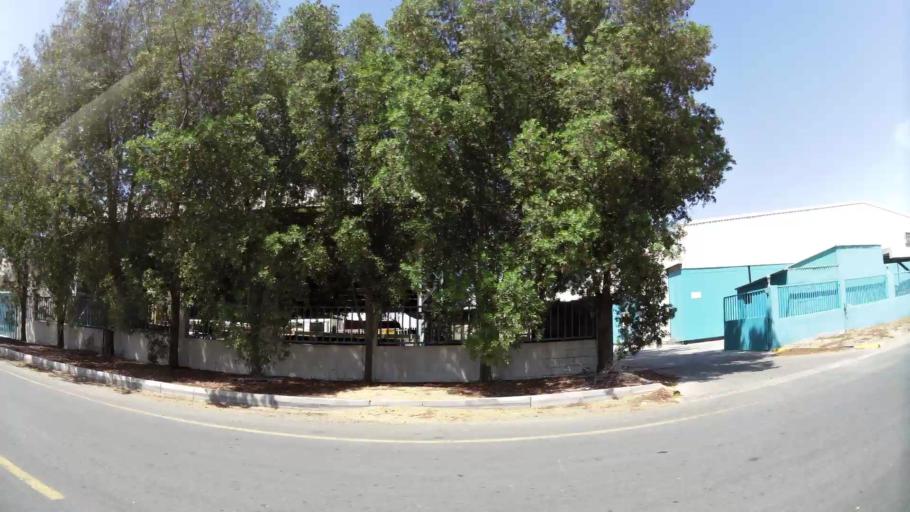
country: AE
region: Dubai
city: Dubai
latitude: 24.9879
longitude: 55.1592
